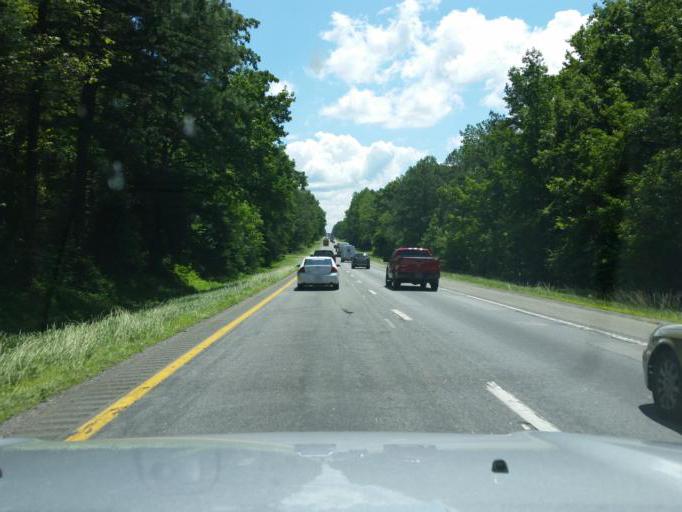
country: US
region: Virginia
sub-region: Henrico County
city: Sandston
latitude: 37.5146
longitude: -77.1791
